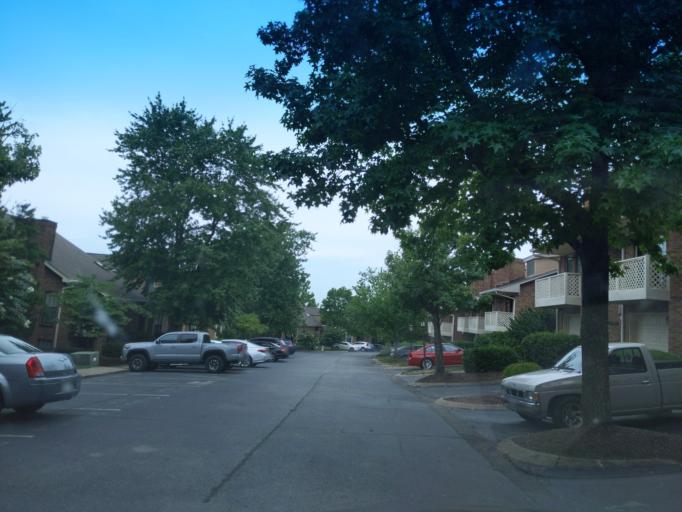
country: US
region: Tennessee
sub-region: Williamson County
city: Brentwood
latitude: 36.0346
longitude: -86.7772
